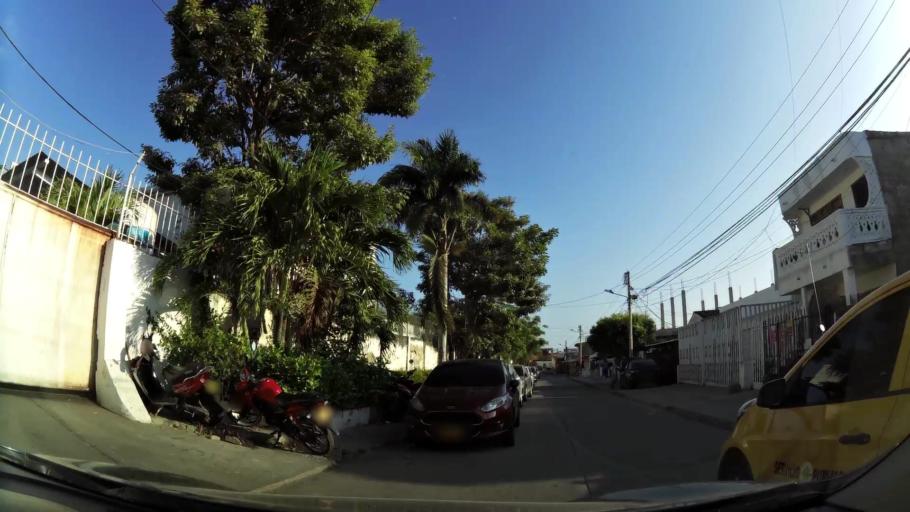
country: CO
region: Bolivar
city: Cartagena
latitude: 10.4064
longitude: -75.5166
